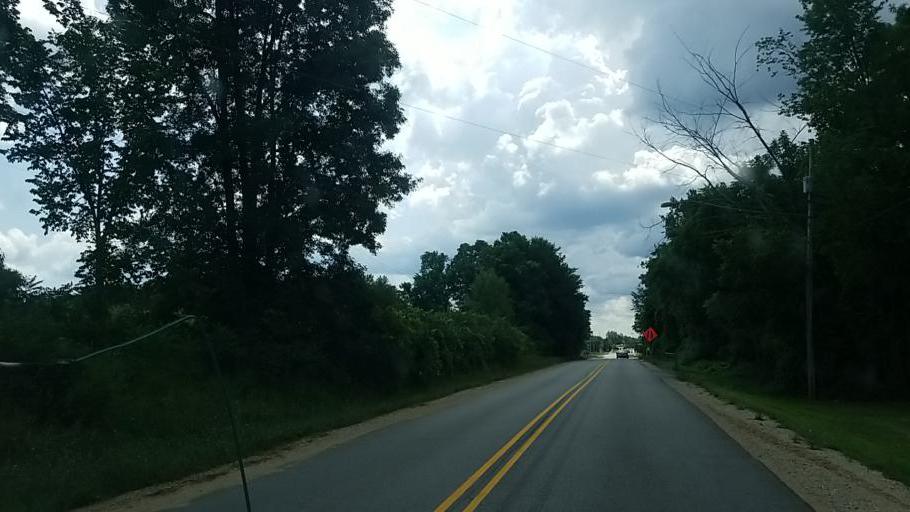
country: US
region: Michigan
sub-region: Kent County
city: Walker
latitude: 43.0281
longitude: -85.7294
